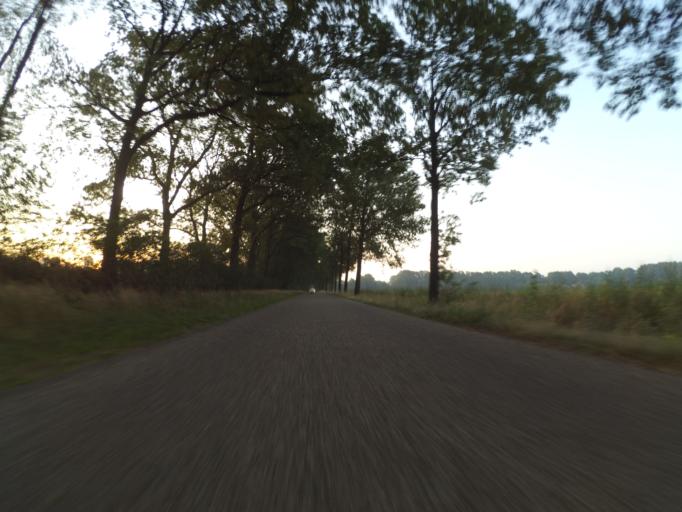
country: DE
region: Lower Saxony
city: Getelo
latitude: 52.3984
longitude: 6.8646
